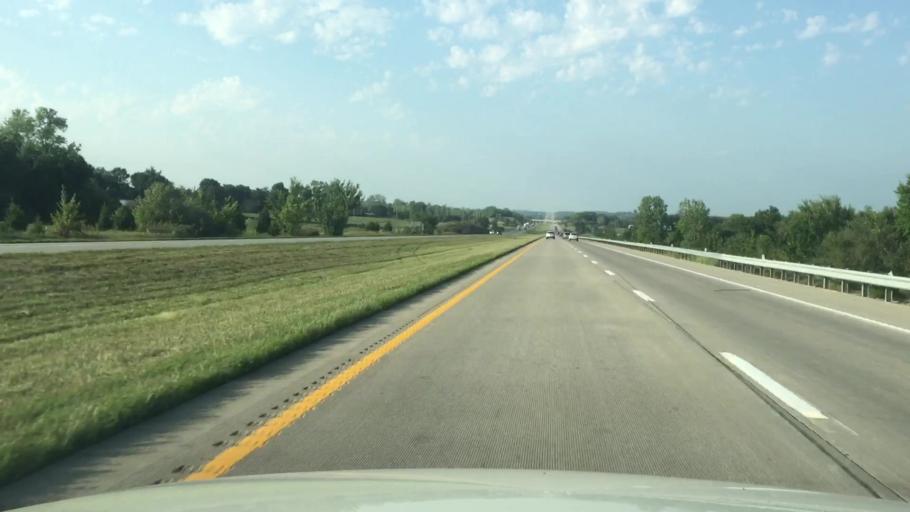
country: US
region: Missouri
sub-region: Clinton County
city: Cameron
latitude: 39.6515
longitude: -94.2397
